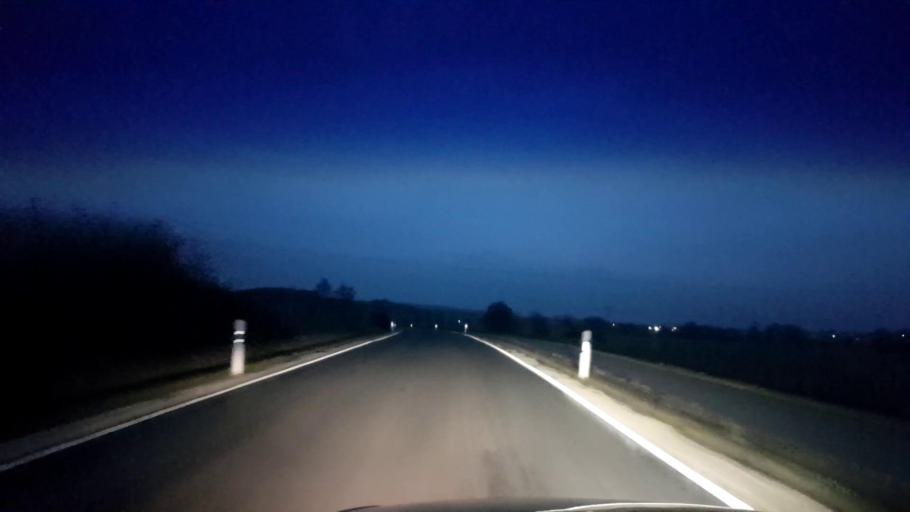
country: DE
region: Bavaria
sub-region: Upper Franconia
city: Burgebrach
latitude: 49.8330
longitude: 10.7533
